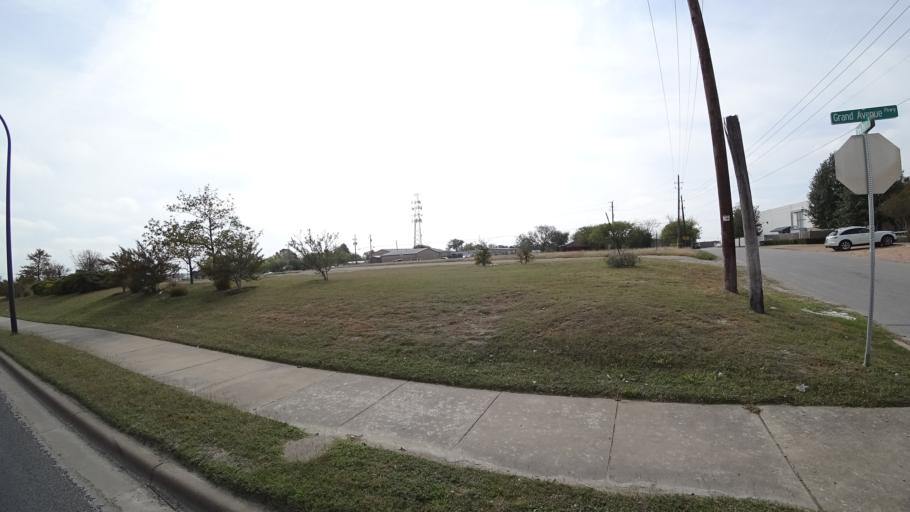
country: US
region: Texas
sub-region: Travis County
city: Wells Branch
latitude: 30.4561
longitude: -97.6695
